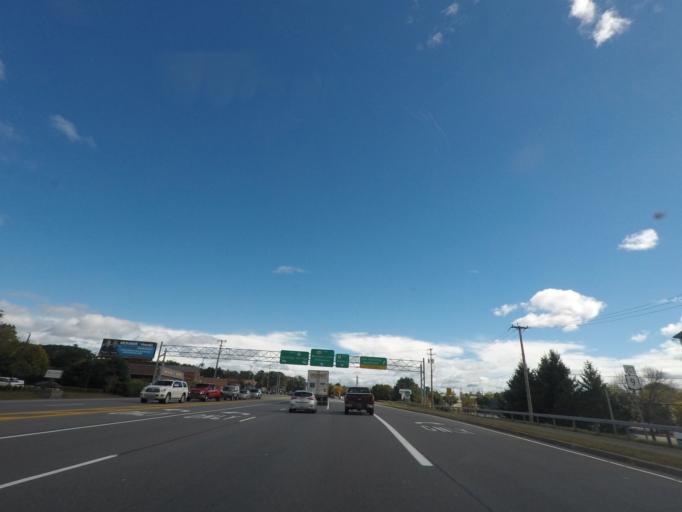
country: US
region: New York
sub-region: Saratoga County
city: Country Knolls
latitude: 42.8627
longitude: -73.7715
